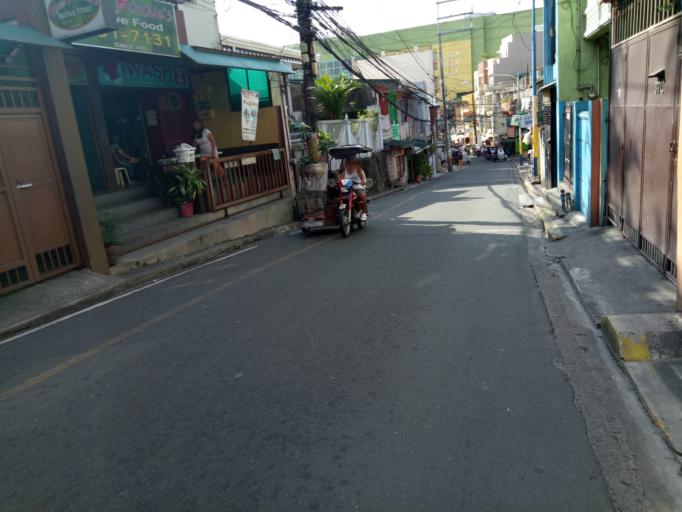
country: PH
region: Metro Manila
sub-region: San Juan
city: San Juan
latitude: 14.5909
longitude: 121.0267
